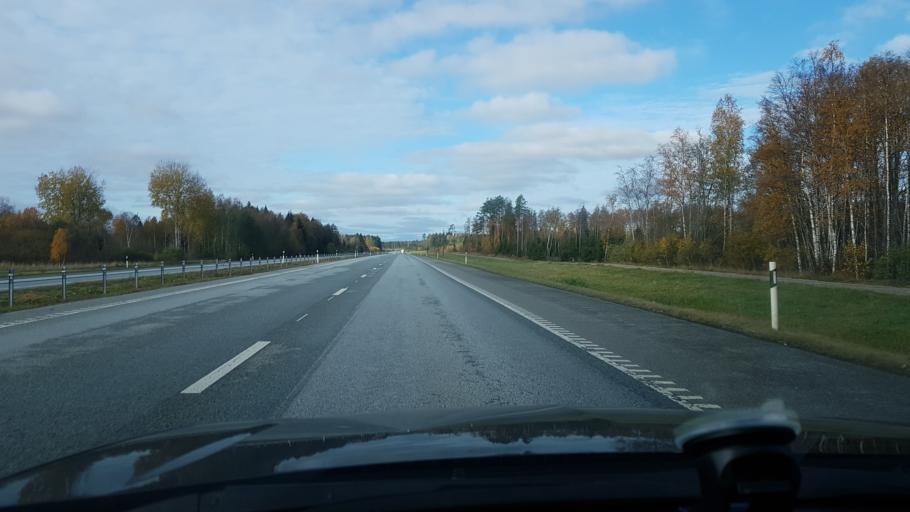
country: EE
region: Laeaene-Virumaa
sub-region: Kadrina vald
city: Kadrina
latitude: 59.4533
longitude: 26.0568
